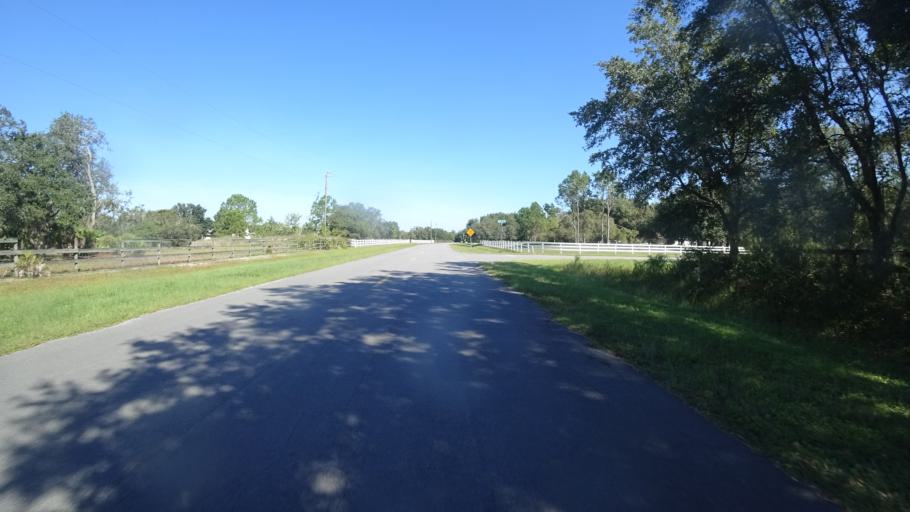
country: US
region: Florida
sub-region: Sarasota County
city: Lake Sarasota
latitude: 27.3631
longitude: -82.2509
